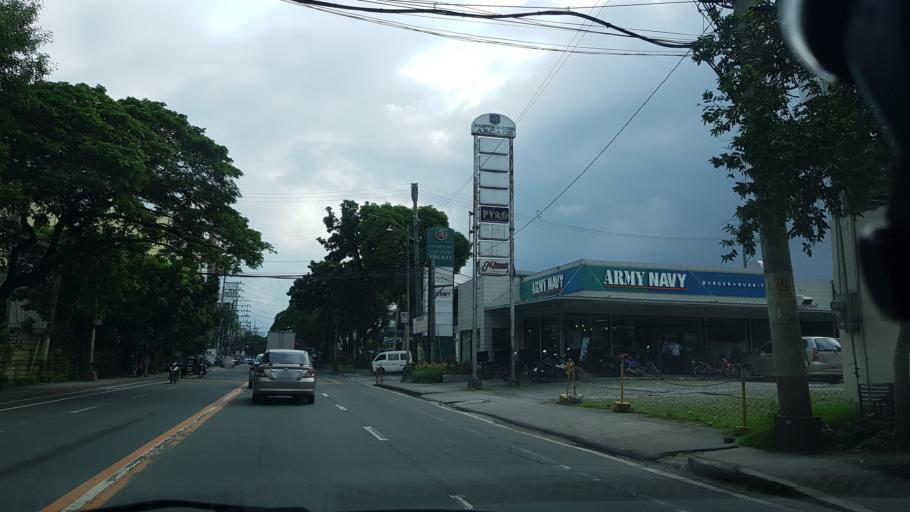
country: PH
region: Metro Manila
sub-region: Pasig
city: Pasig City
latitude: 14.5783
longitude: 121.0861
